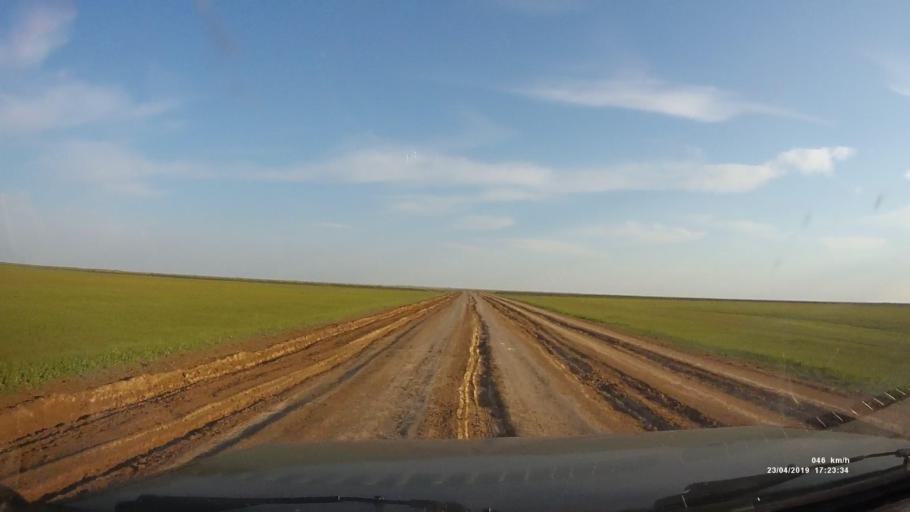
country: RU
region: Kalmykiya
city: Priyutnoye
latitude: 46.1612
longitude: 43.5079
